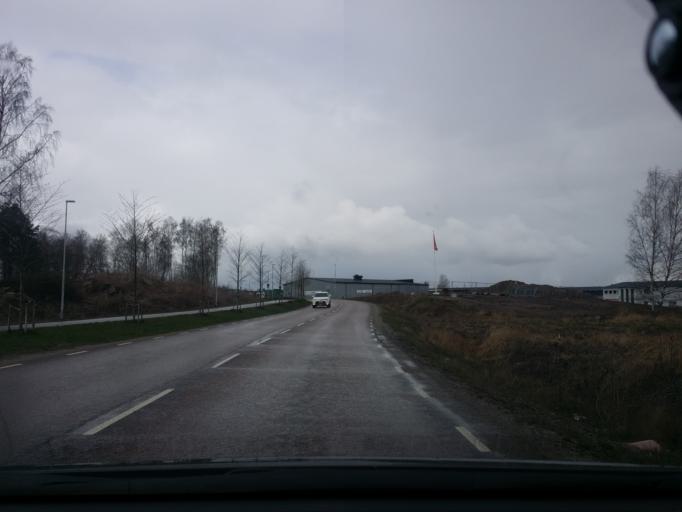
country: SE
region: Uppsala
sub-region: Enkopings Kommun
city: Enkoping
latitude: 59.6457
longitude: 17.0928
